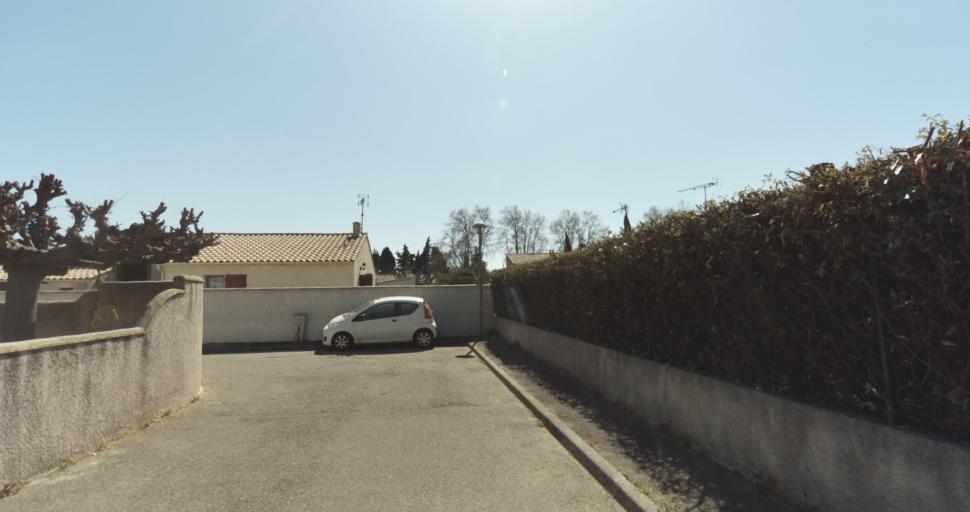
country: FR
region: Provence-Alpes-Cote d'Azur
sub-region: Departement des Bouches-du-Rhone
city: Pelissanne
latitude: 43.6307
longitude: 5.1650
